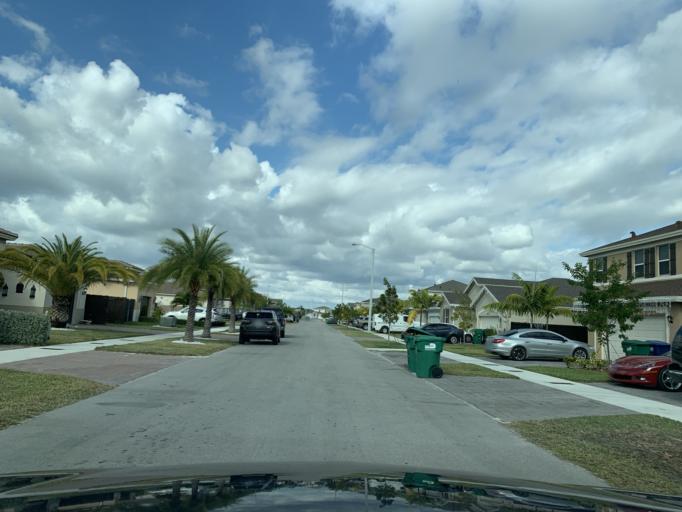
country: US
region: Florida
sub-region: Miami-Dade County
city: Naranja
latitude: 25.5094
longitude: -80.4089
